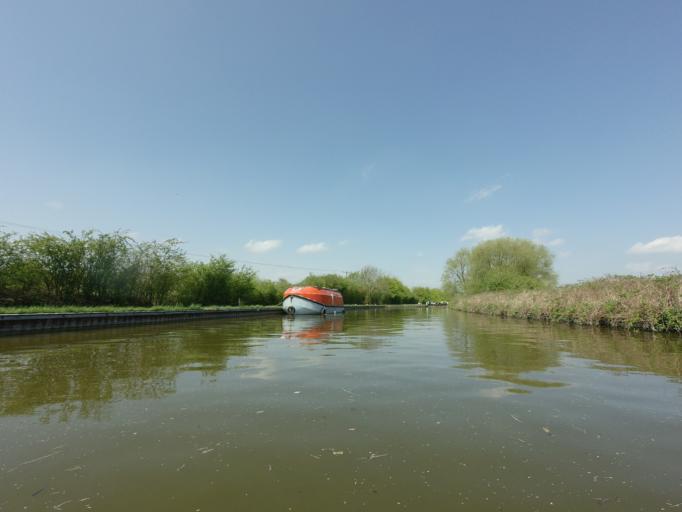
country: GB
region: England
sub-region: Buckinghamshire
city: Cheddington
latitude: 51.8566
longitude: -0.6464
